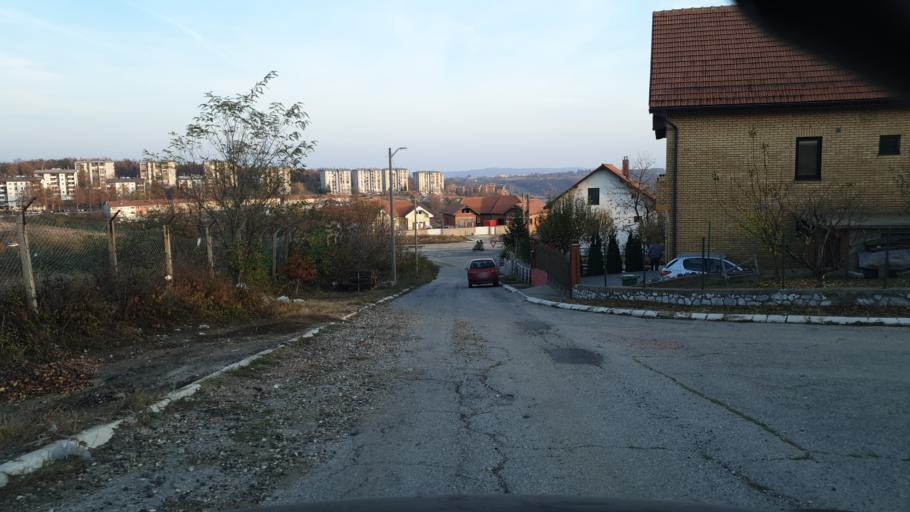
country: RS
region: Central Serbia
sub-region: Borski Okrug
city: Bor
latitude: 44.0590
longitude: 22.0883
